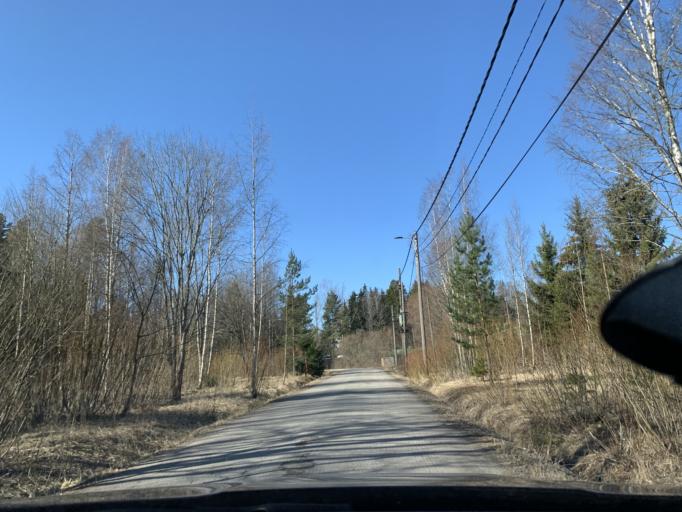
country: FI
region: Uusimaa
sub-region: Helsinki
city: Espoo
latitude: 60.1705
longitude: 24.5858
